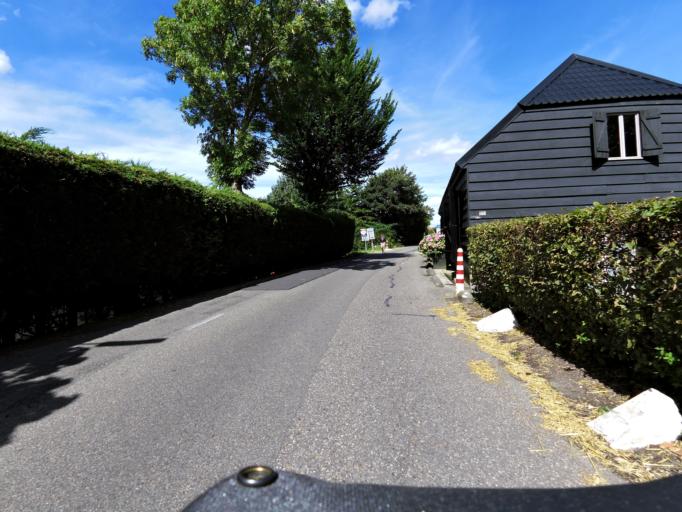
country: NL
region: South Holland
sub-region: Gemeente Zwijndrecht
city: Heerjansdam
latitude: 51.8370
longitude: 4.5563
